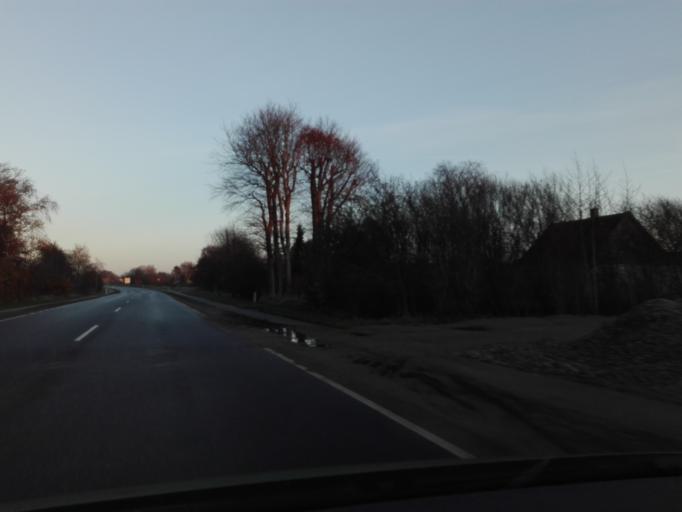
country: DK
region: Central Jutland
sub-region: Arhus Kommune
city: Framlev
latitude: 56.1513
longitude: 9.9927
